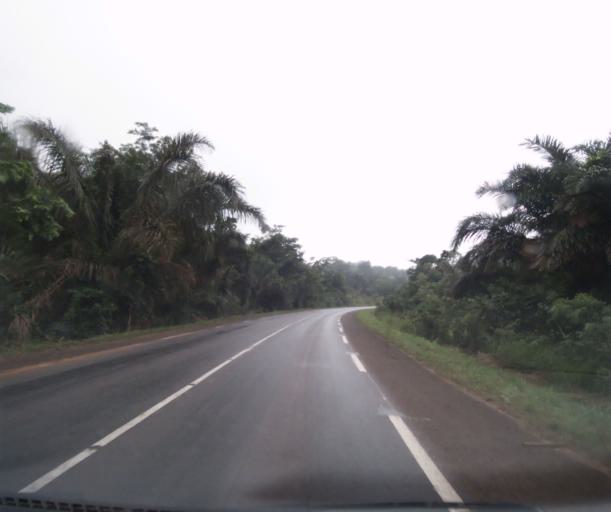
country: CM
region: Centre
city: Mbankomo
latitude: 3.7639
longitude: 11.1925
